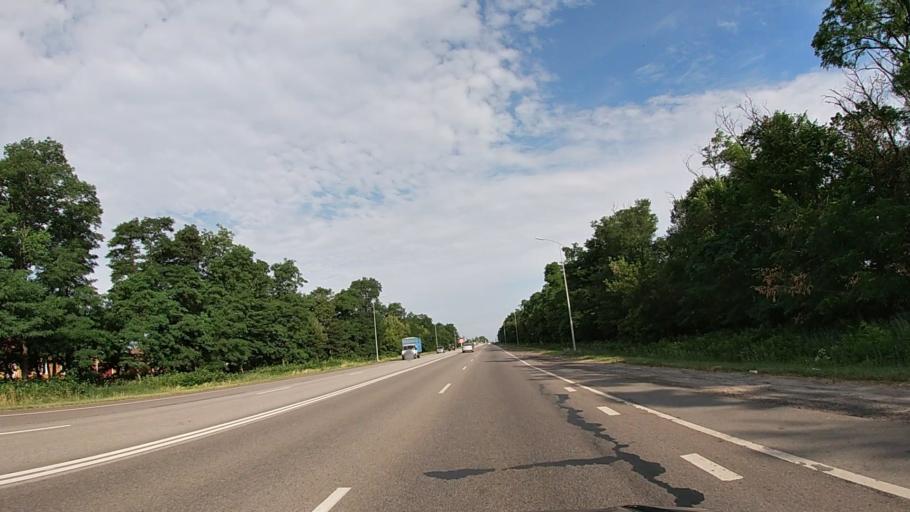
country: RU
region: Belgorod
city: Severnyy
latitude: 50.6396
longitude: 36.4402
